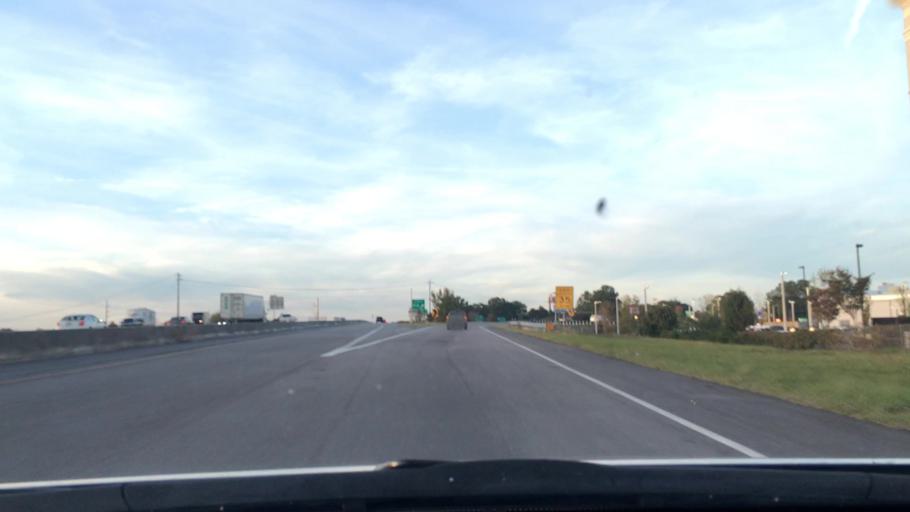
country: US
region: South Carolina
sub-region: Richland County
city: Forest Acres
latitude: 33.9697
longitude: -80.9537
